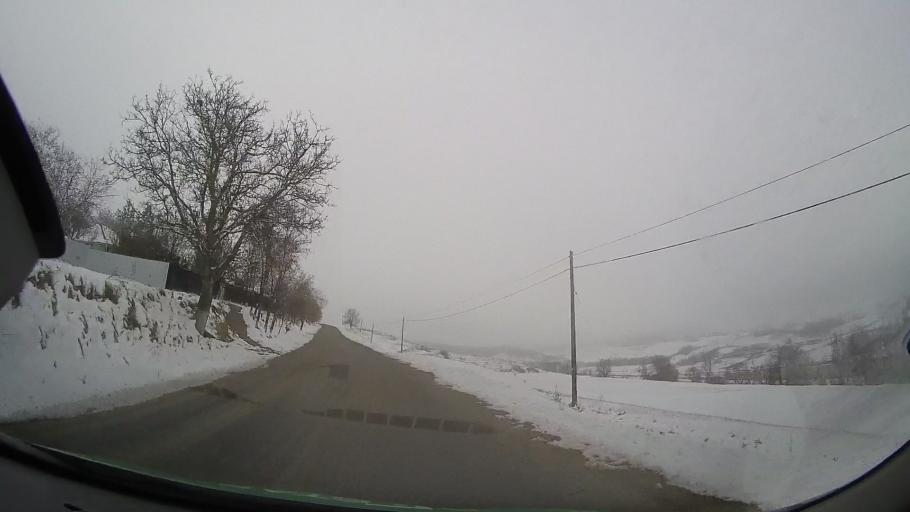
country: RO
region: Bacau
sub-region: Comuna Vultureni
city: Vultureni
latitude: 46.3789
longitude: 27.2757
